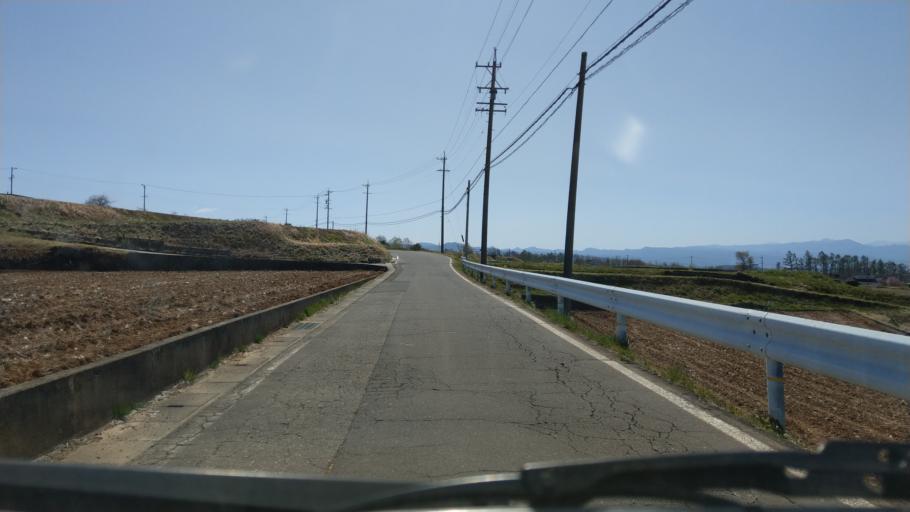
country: JP
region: Nagano
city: Komoro
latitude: 36.3545
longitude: 138.3968
